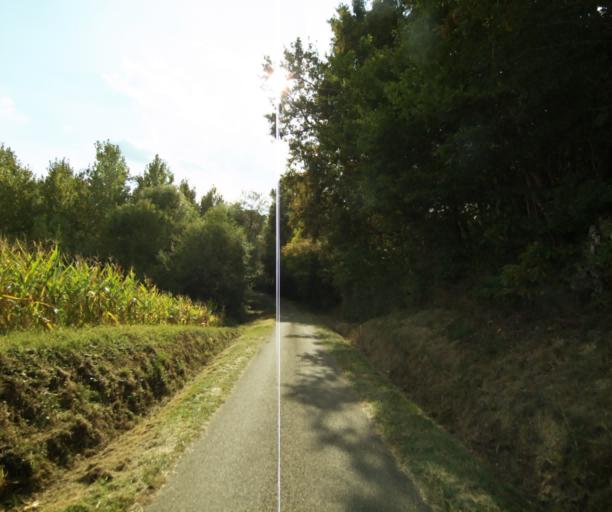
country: FR
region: Midi-Pyrenees
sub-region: Departement du Gers
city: Cazaubon
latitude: 43.8830
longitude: -0.0532
